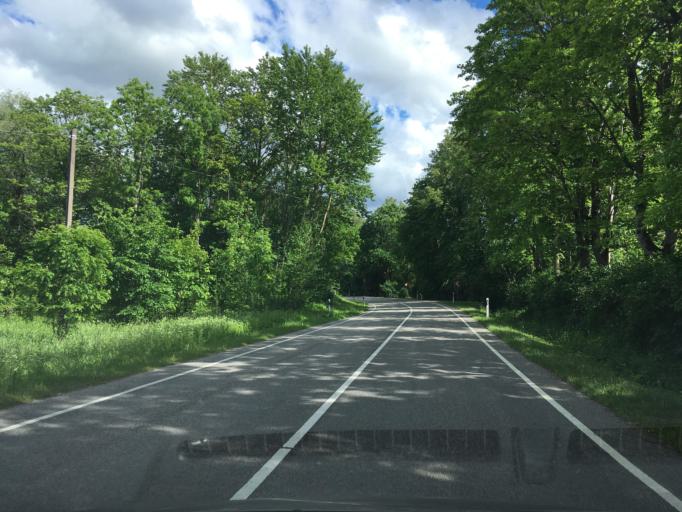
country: EE
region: Paernumaa
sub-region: Halinga vald
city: Parnu-Jaagupi
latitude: 58.6737
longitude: 24.6220
